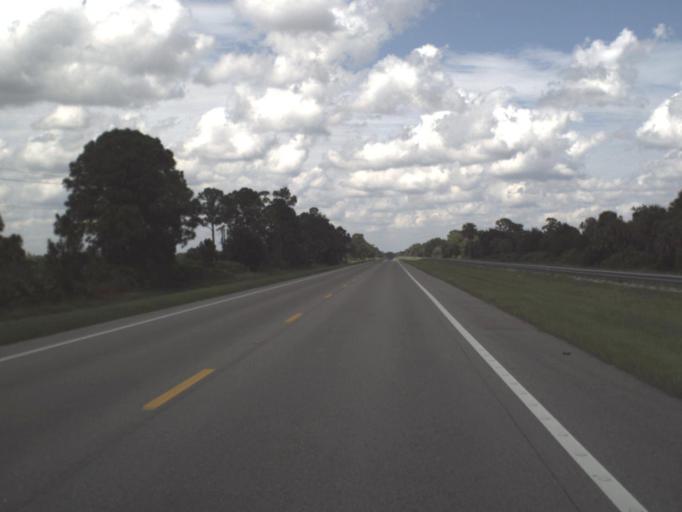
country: US
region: Florida
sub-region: Collier County
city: Immokalee
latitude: 26.3338
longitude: -81.3433
